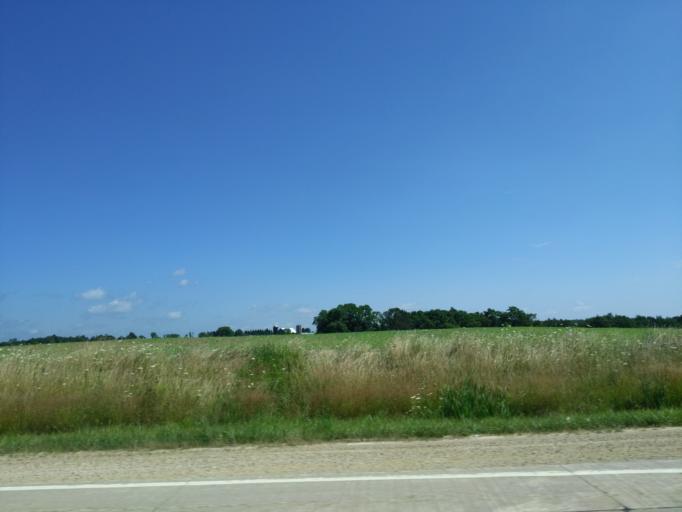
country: US
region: Wisconsin
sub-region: La Crosse County
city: West Salem
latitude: 43.7187
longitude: -91.0784
